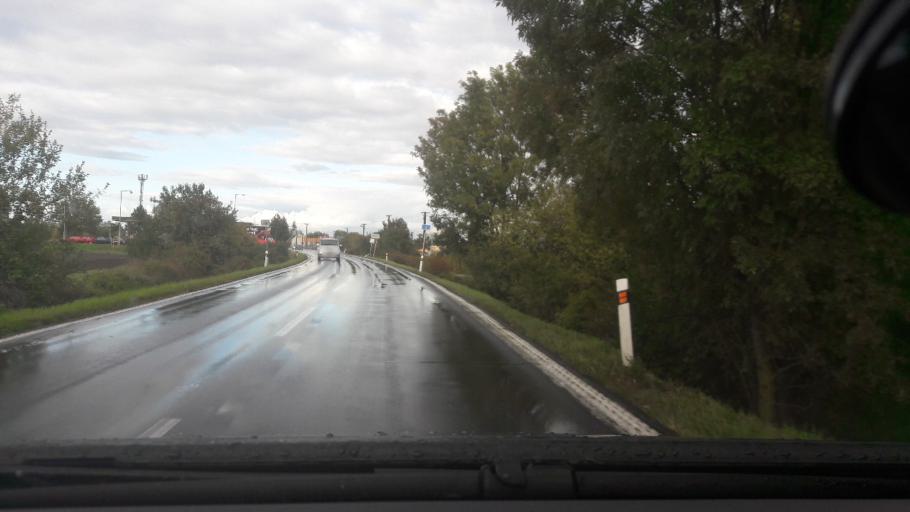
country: CZ
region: South Moravian
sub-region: Okres Breclav
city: Lanzhot
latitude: 48.6473
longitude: 17.0110
